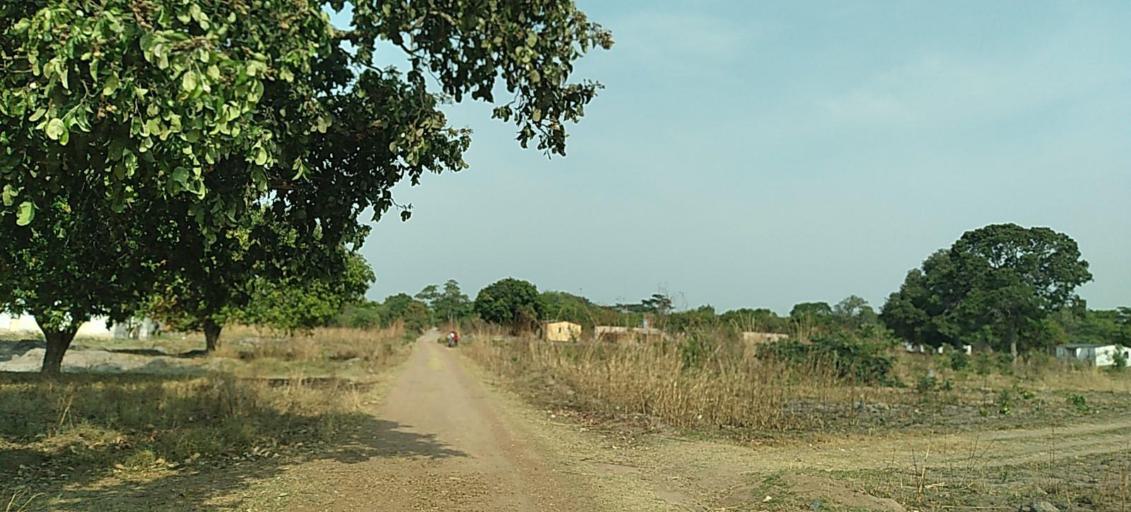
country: ZM
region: Copperbelt
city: Ndola
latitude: -13.2221
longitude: 28.6702
